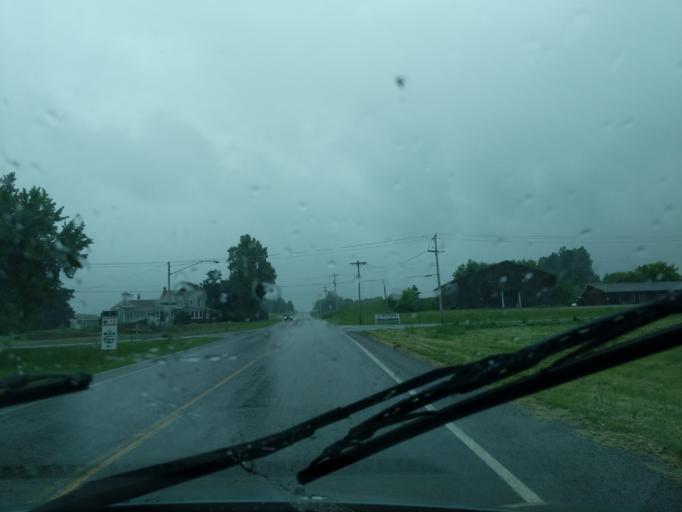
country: US
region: Michigan
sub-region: Berrien County
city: Coloma
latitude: 42.1724
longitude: -86.3065
